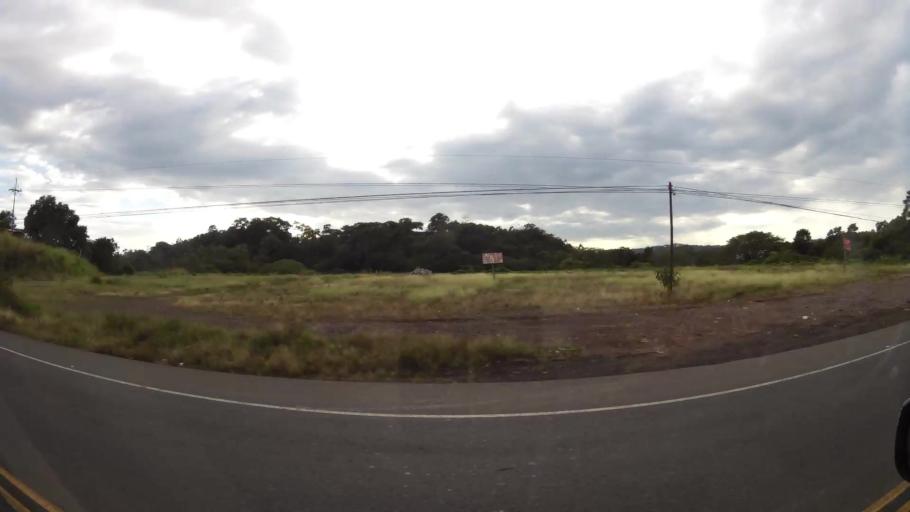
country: CR
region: Puntarenas
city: Esparza
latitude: 9.9042
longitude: -84.6604
